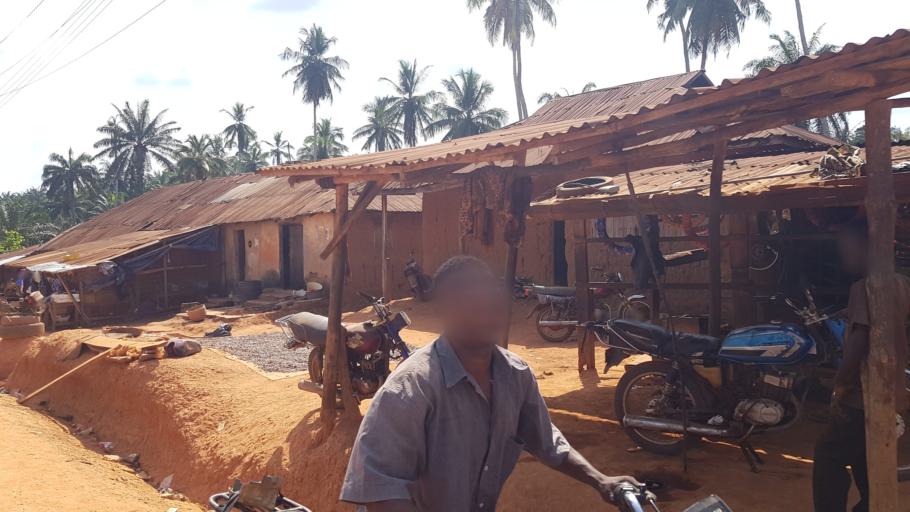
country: NG
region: Osun
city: Ifetedo
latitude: 7.0201
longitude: 4.6317
